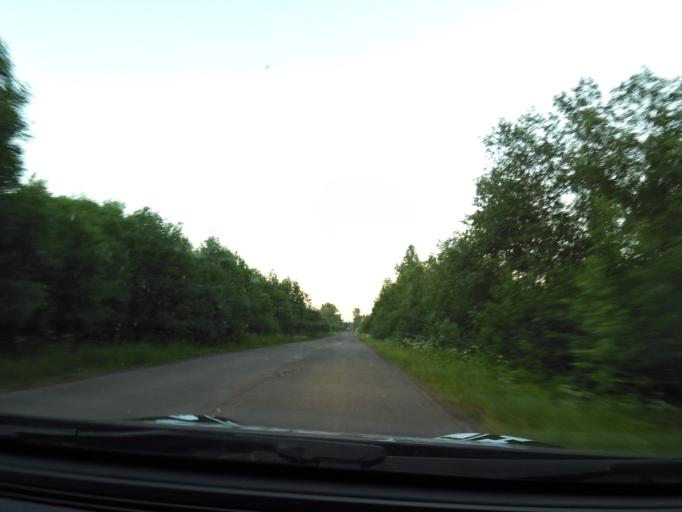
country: RU
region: Leningrad
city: Voznesen'ye
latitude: 60.8262
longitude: 35.7201
